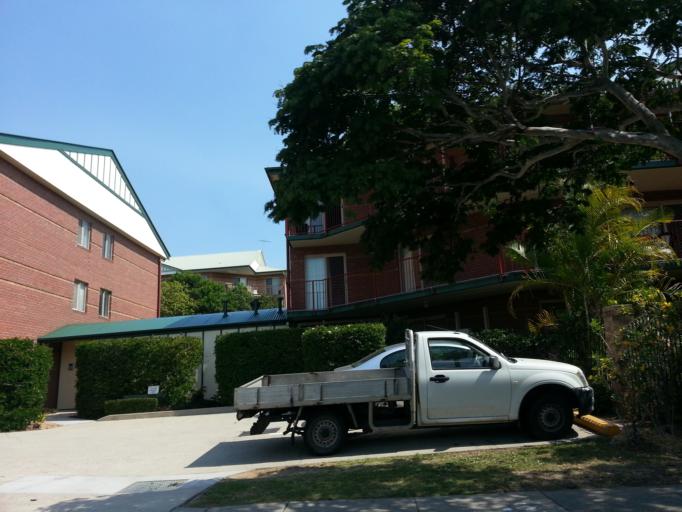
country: AU
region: Queensland
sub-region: Brisbane
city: Wooloowin
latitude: -27.4217
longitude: 153.0362
